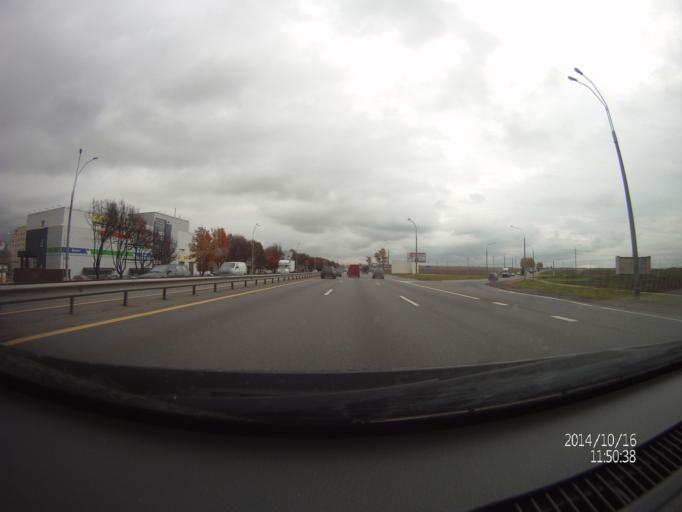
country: BY
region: Minsk
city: Machulishchy
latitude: 53.8333
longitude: 27.6064
